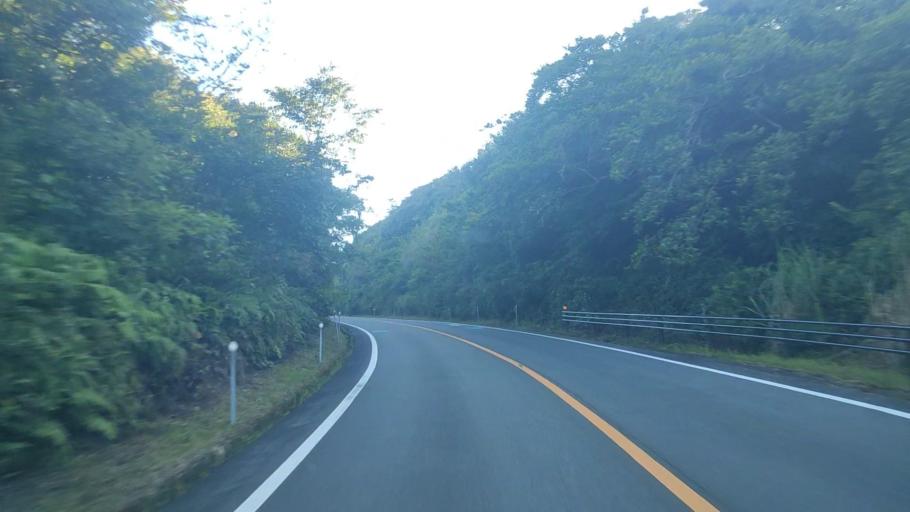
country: JP
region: Mie
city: Toba
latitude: 34.4123
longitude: 136.9031
